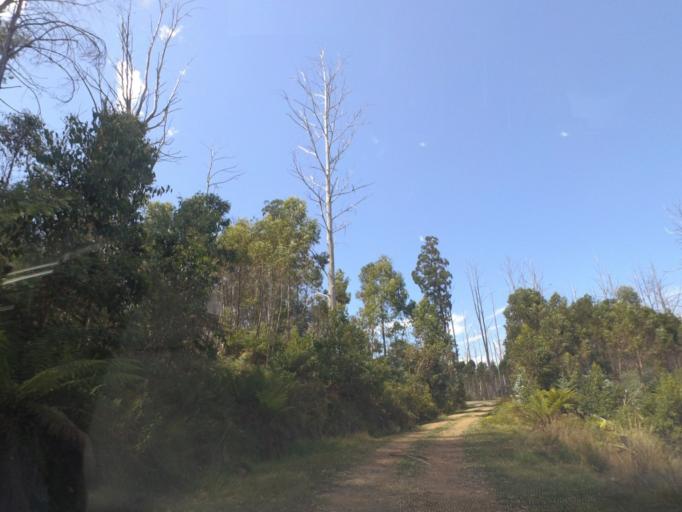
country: AU
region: Victoria
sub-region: Murrindindi
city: Alexandra
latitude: -37.4804
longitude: 145.8387
